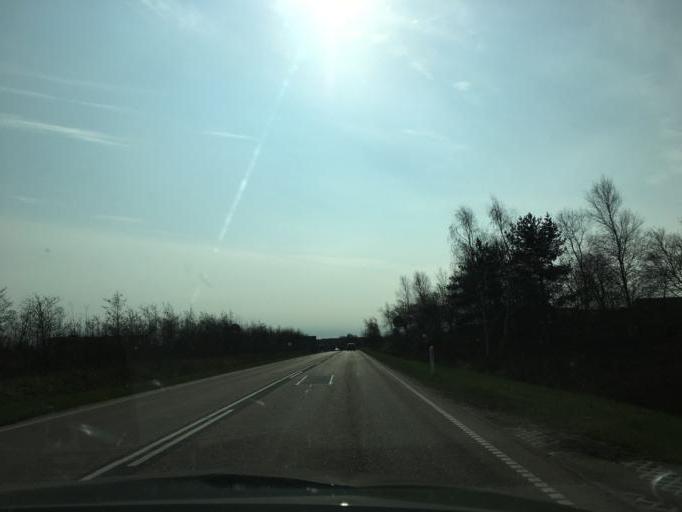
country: DK
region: South Denmark
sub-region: Vejen Kommune
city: Vejen
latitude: 55.4891
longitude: 9.1319
